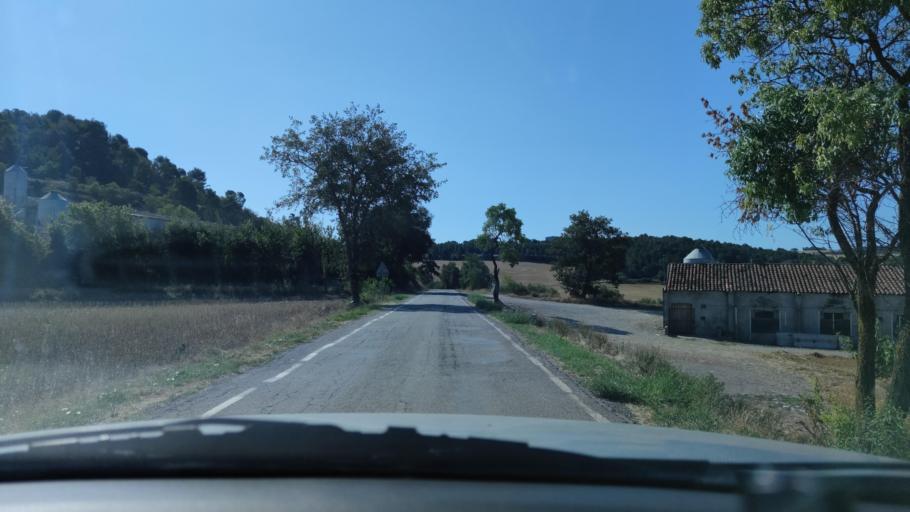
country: ES
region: Catalonia
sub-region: Provincia de Barcelona
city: Pujalt
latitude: 41.6900
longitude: 1.3805
